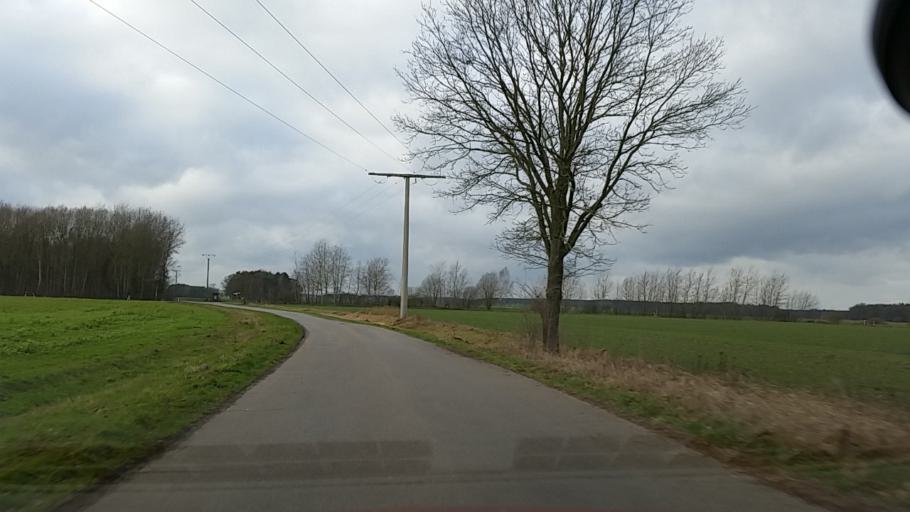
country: DE
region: Lower Saxony
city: Luder
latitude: 52.7641
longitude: 10.6687
